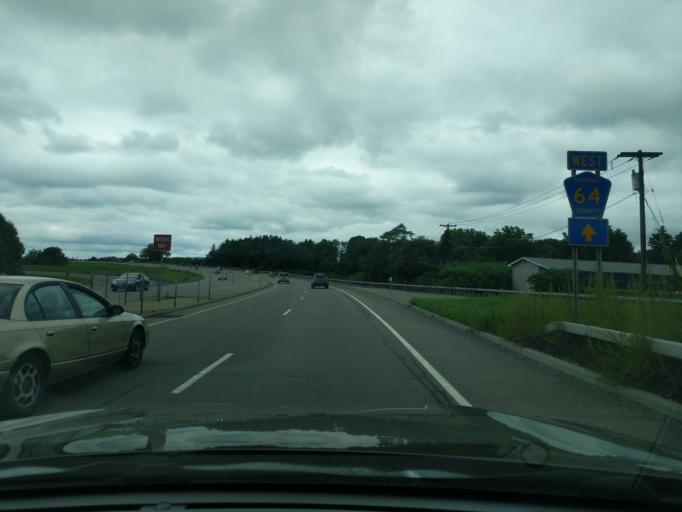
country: US
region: New York
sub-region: Chemung County
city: Horseheads
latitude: 42.1633
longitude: -76.8406
